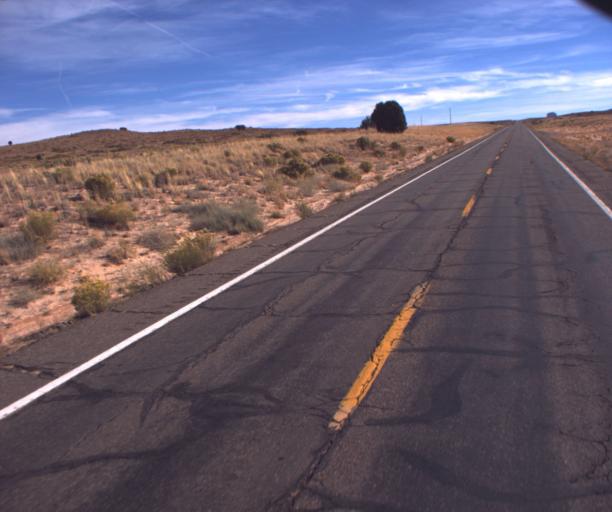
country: US
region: Arizona
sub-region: Coconino County
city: Kaibito
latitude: 36.6130
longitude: -111.0555
